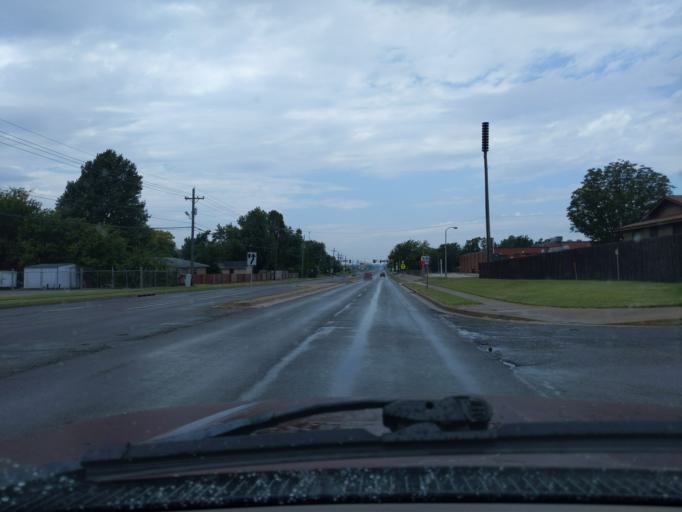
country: US
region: Oklahoma
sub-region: Tulsa County
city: Broken Arrow
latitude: 36.1335
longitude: -95.8393
